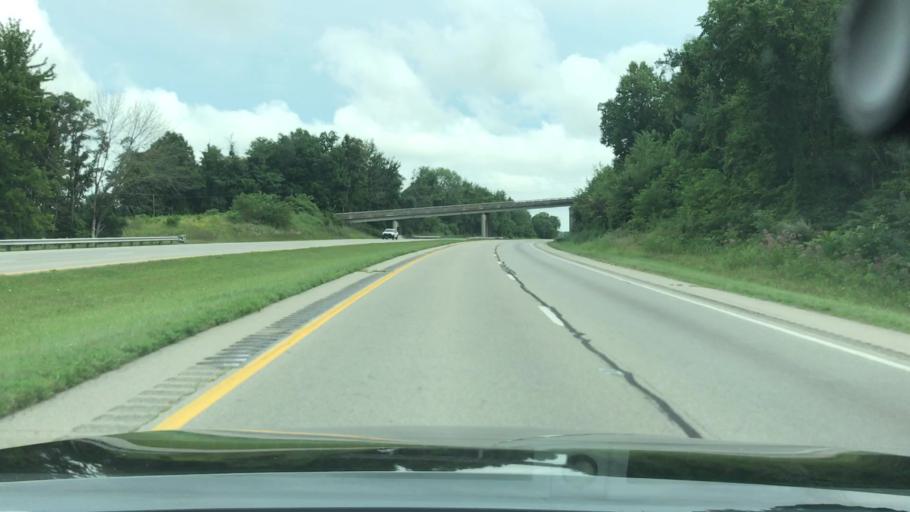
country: US
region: Ohio
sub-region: Jackson County
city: Oak Hill
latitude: 38.9664
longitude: -82.4994
